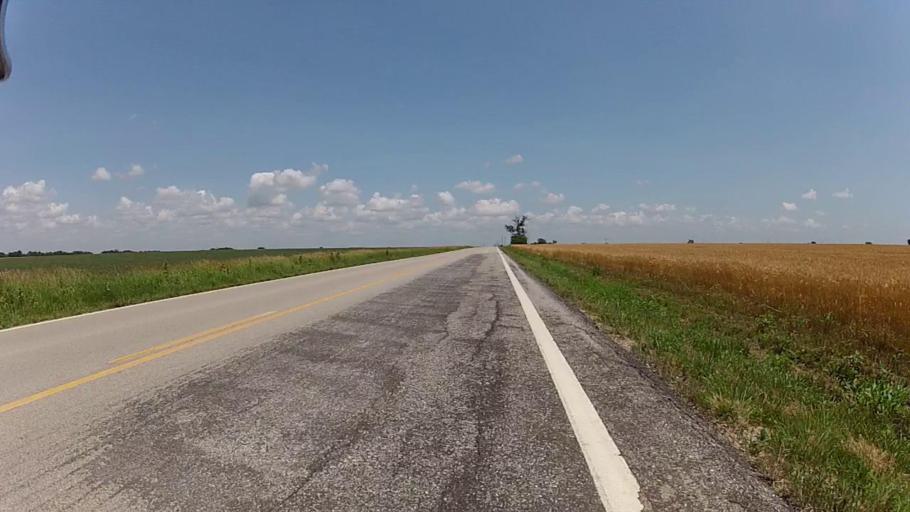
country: US
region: Kansas
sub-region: Labette County
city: Altamont
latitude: 37.1923
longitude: -95.4351
